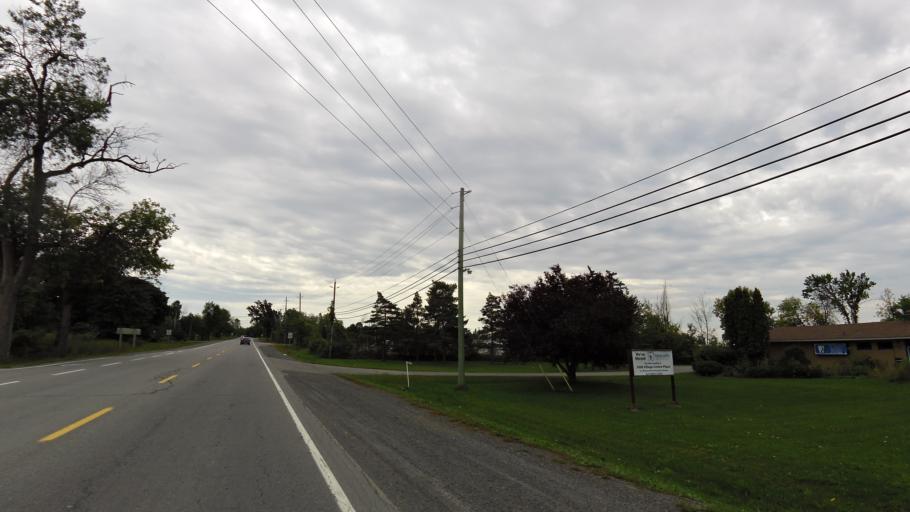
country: CA
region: Ontario
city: Ottawa
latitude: 45.2393
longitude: -75.5148
